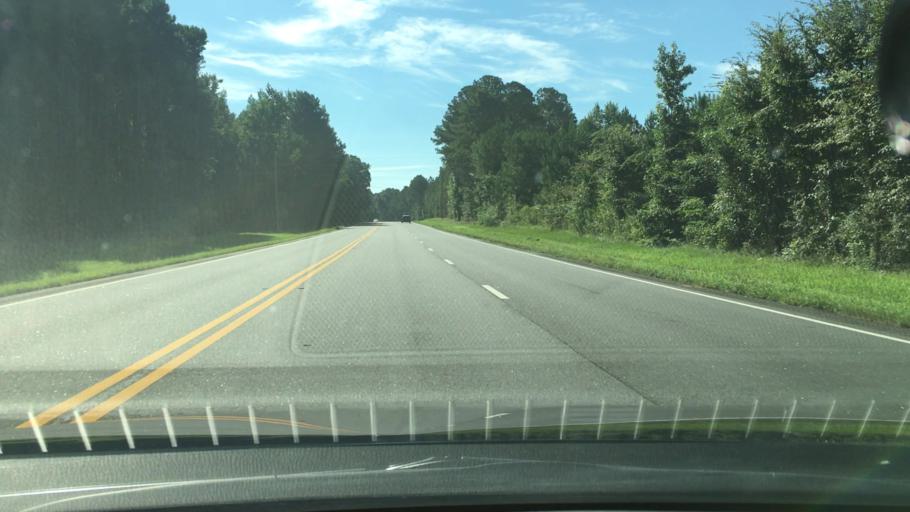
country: US
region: Georgia
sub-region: Putnam County
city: Jefferson
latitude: 33.4413
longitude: -83.3975
